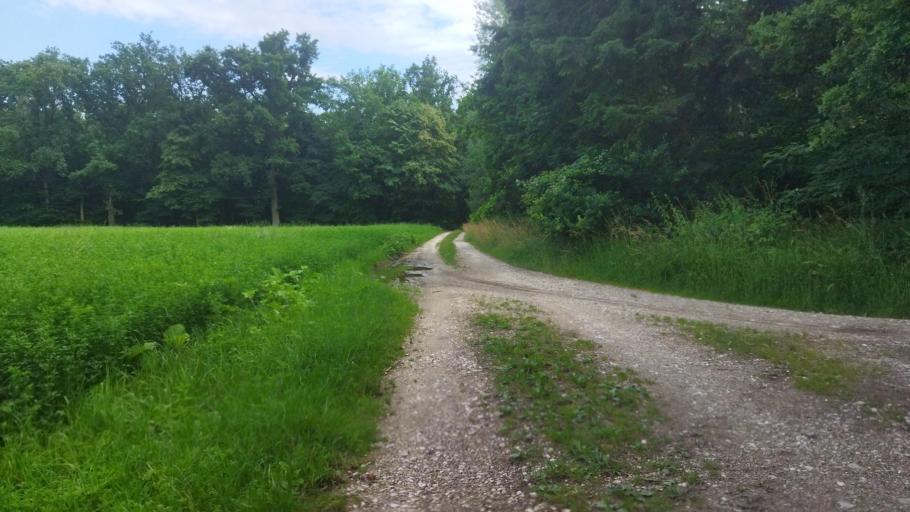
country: DE
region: Bavaria
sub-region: Upper Palatinate
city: Mintraching
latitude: 48.9701
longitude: 12.2987
